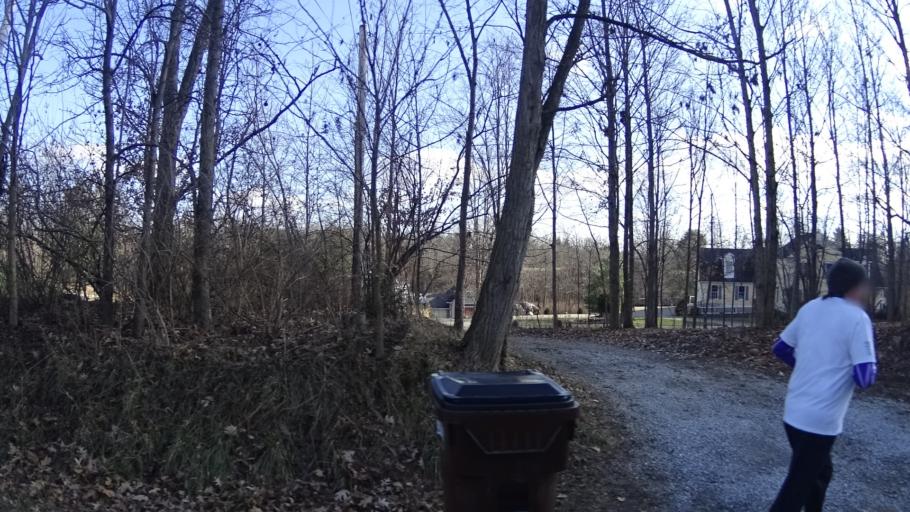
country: US
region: Ohio
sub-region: Lorain County
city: Camden
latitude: 41.1866
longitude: -82.2834
